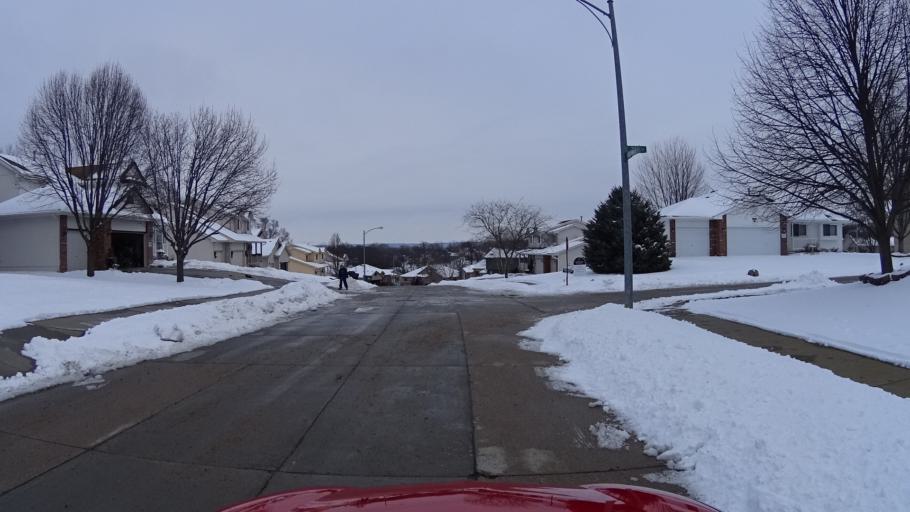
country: US
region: Nebraska
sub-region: Sarpy County
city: Offutt Air Force Base
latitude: 41.1105
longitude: -95.9436
